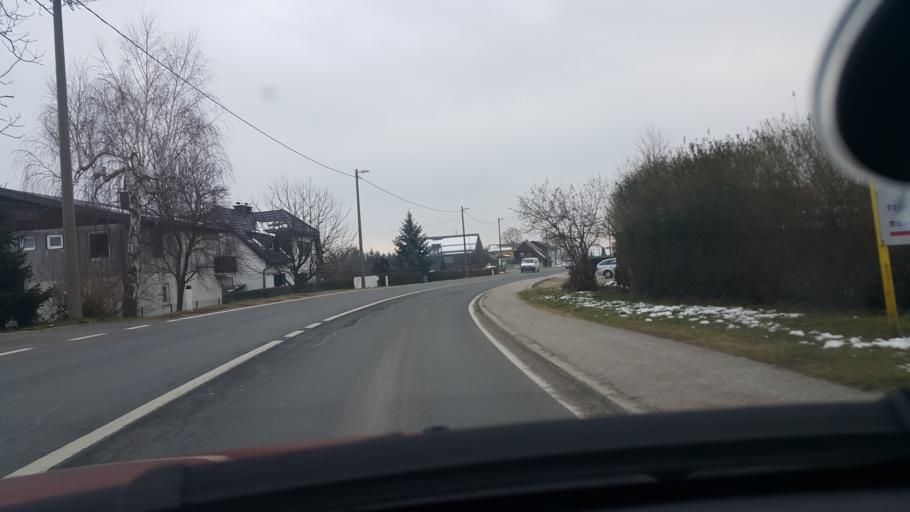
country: SI
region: Hoce-Slivnica
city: Radizel
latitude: 46.4679
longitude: 15.6574
